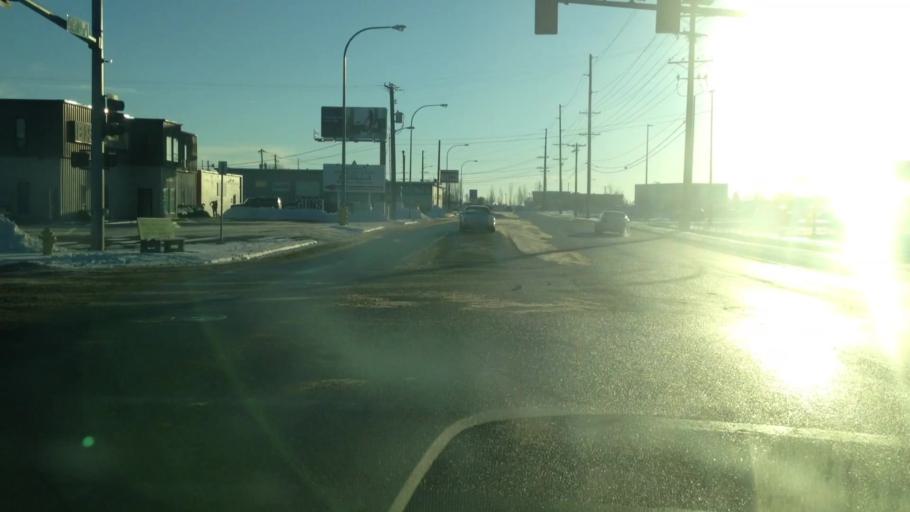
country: US
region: Idaho
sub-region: Bonneville County
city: Idaho Falls
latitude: 43.4927
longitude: -112.0495
